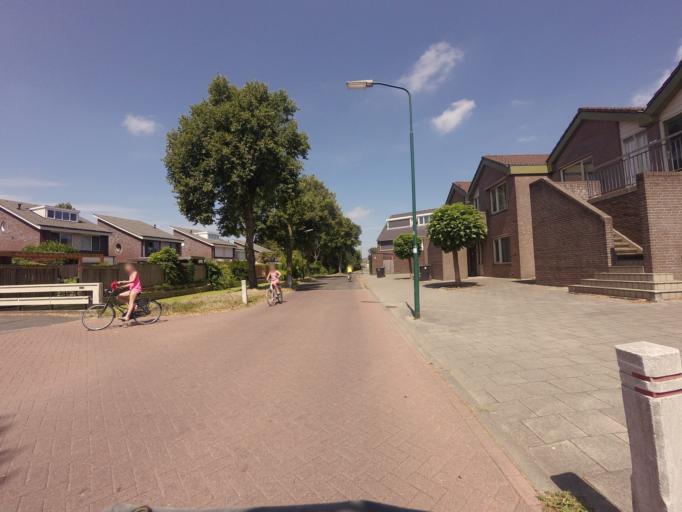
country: NL
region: Utrecht
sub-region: Gemeente Montfoort
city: Montfoort
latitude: 52.0883
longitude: 4.9578
